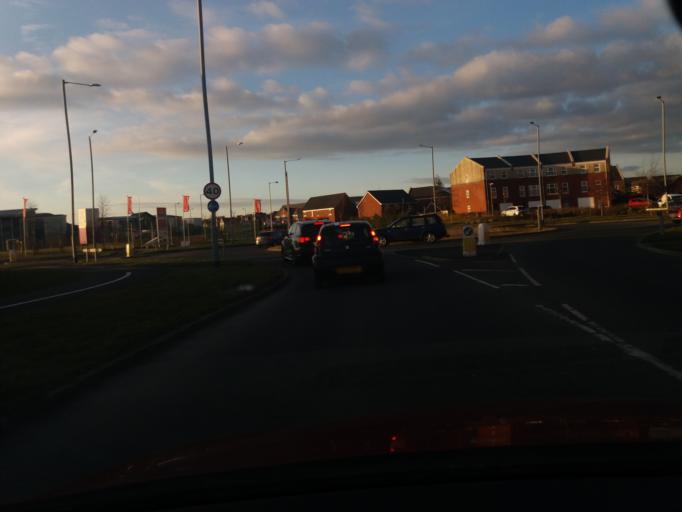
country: GB
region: England
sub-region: Lancashire
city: Euxton
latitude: 53.6768
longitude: -2.6562
